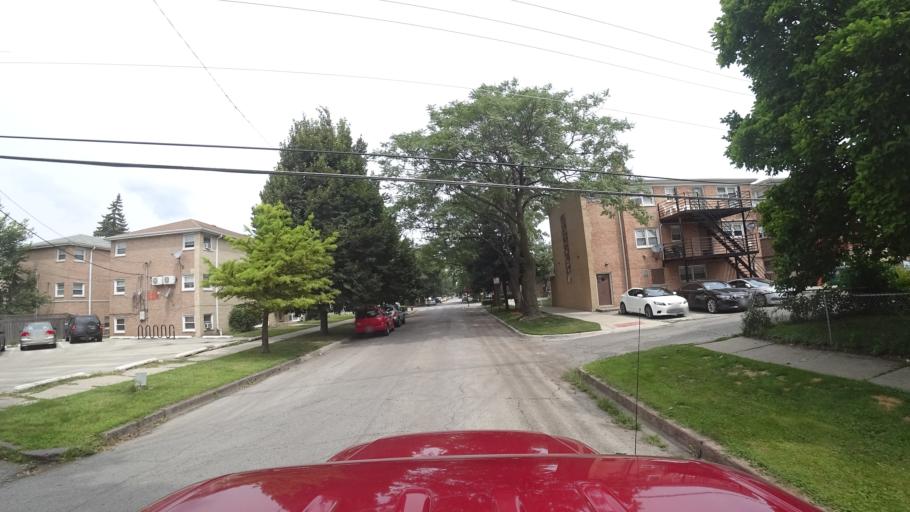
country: US
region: Illinois
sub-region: Cook County
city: Chicago
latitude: 41.8297
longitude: -87.6826
